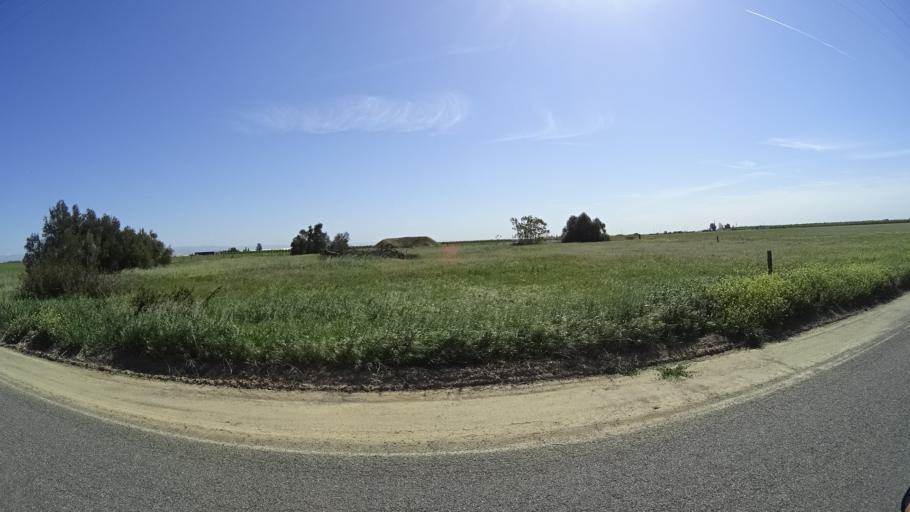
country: US
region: California
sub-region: Glenn County
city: Orland
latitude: 39.6501
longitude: -122.1785
